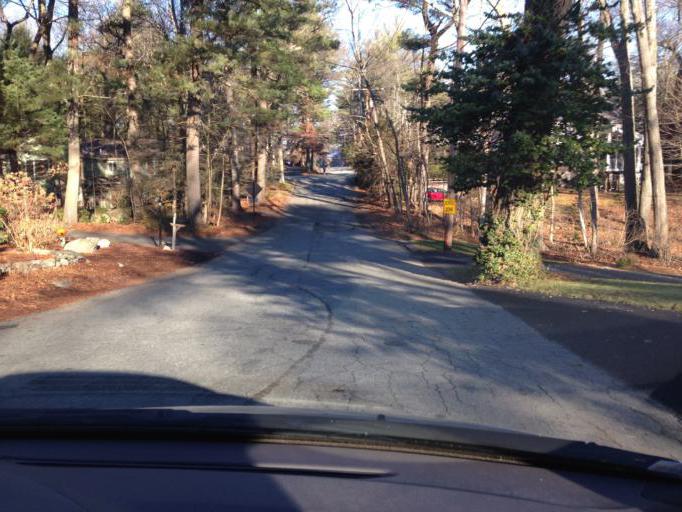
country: US
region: Massachusetts
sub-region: Middlesex County
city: Bedford
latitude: 42.5130
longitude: -71.2778
